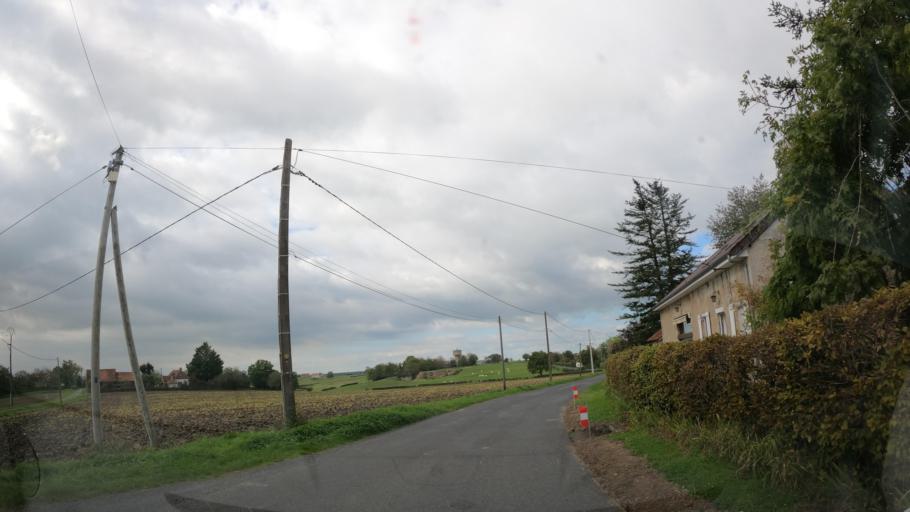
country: FR
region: Auvergne
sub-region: Departement de l'Allier
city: Lapalisse
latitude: 46.3489
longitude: 3.6251
